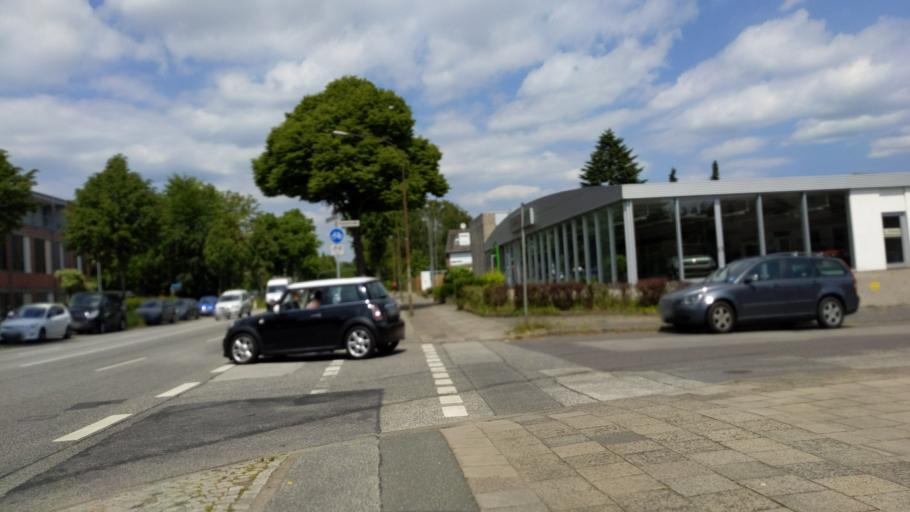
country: DE
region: Schleswig-Holstein
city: Luebeck
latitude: 53.8758
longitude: 10.7085
